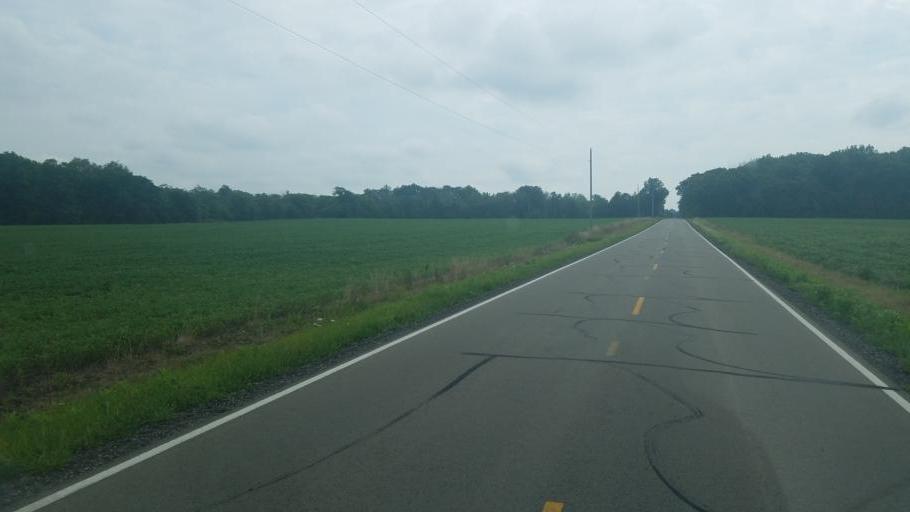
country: US
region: Ohio
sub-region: Crawford County
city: Galion
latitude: 40.7197
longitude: -82.8478
